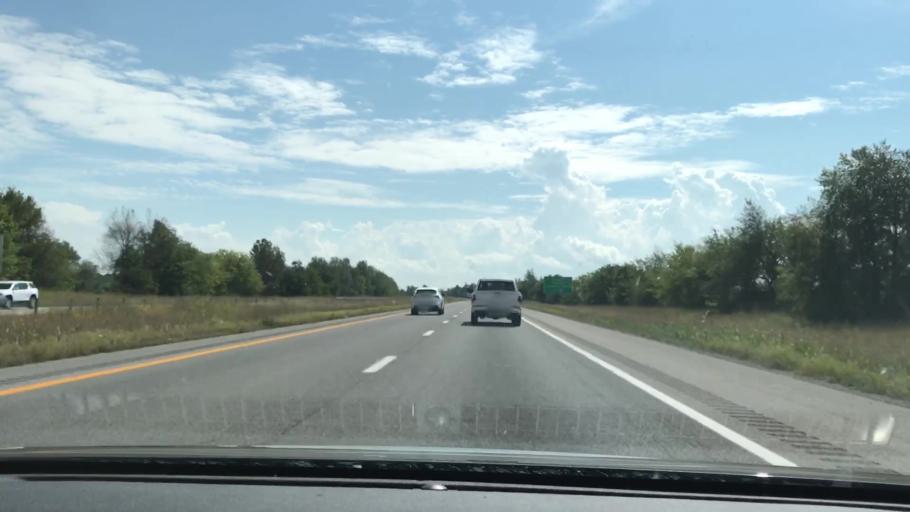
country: US
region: Kentucky
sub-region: Christian County
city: Oak Grove
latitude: 36.7218
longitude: -87.4859
